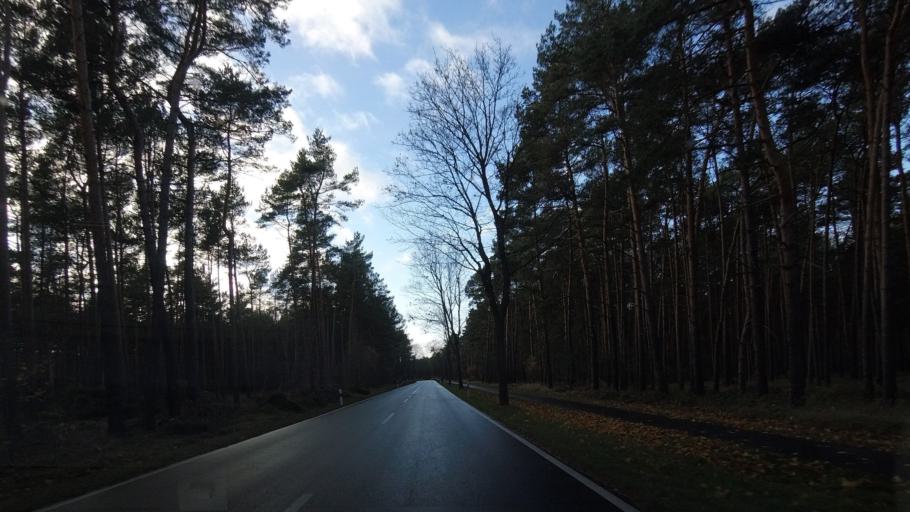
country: DE
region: Brandenburg
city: Linthe
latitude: 52.0950
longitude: 12.7827
